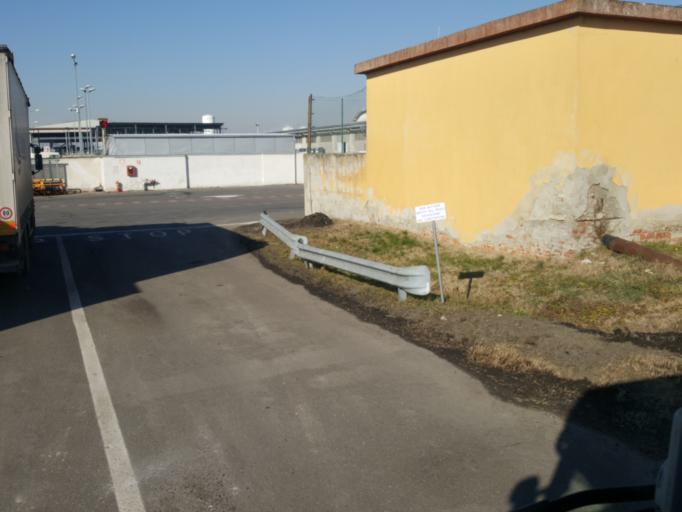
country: IT
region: Piedmont
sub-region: Provincia di Alessandria
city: Castellar Guidobono
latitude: 44.9032
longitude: 8.9419
